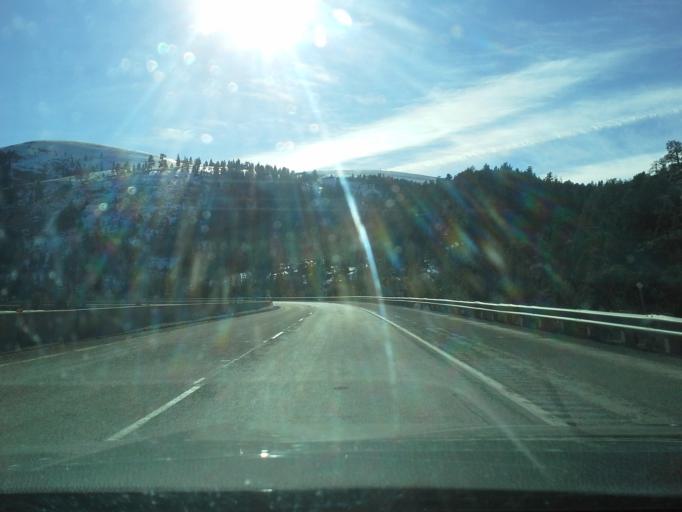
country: US
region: Montana
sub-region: Lewis and Clark County
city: Helena Valley Northwest
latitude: 46.9254
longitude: -112.1230
